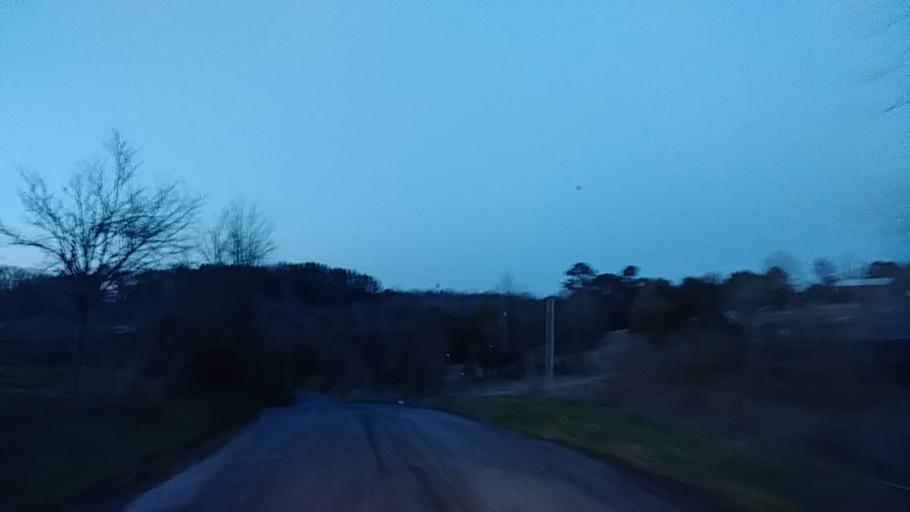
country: US
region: Tennessee
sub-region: Greene County
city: Mosheim
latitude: 36.0700
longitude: -82.9879
